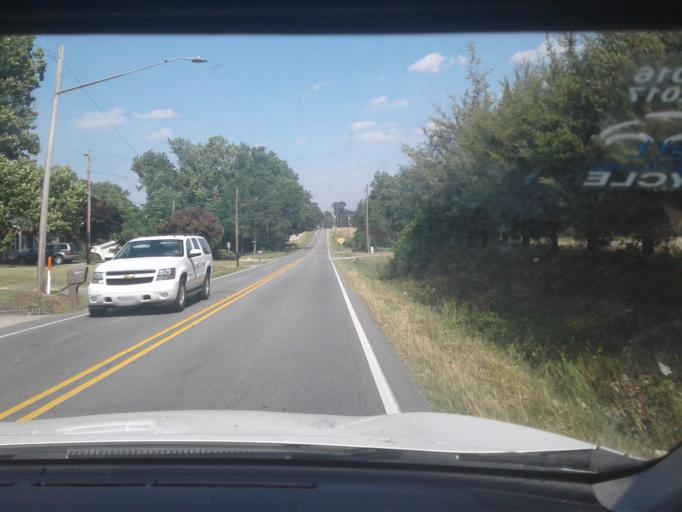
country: US
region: North Carolina
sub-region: Johnston County
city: Benson
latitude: 35.3876
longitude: -78.5648
